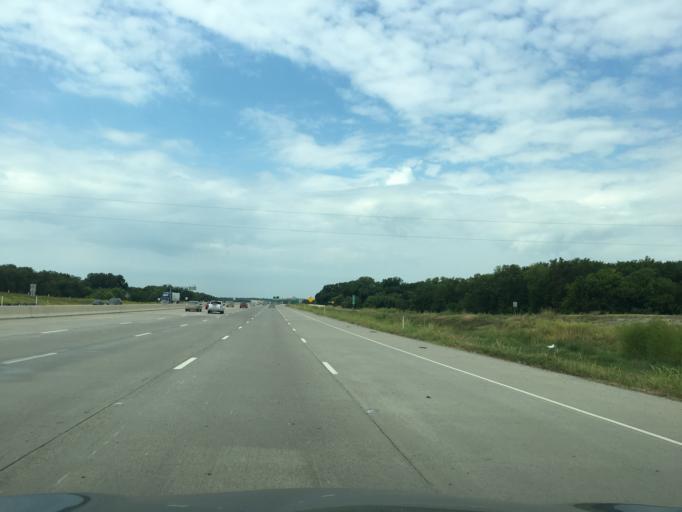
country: US
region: Texas
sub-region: Collin County
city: Melissa
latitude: 33.2602
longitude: -96.6058
